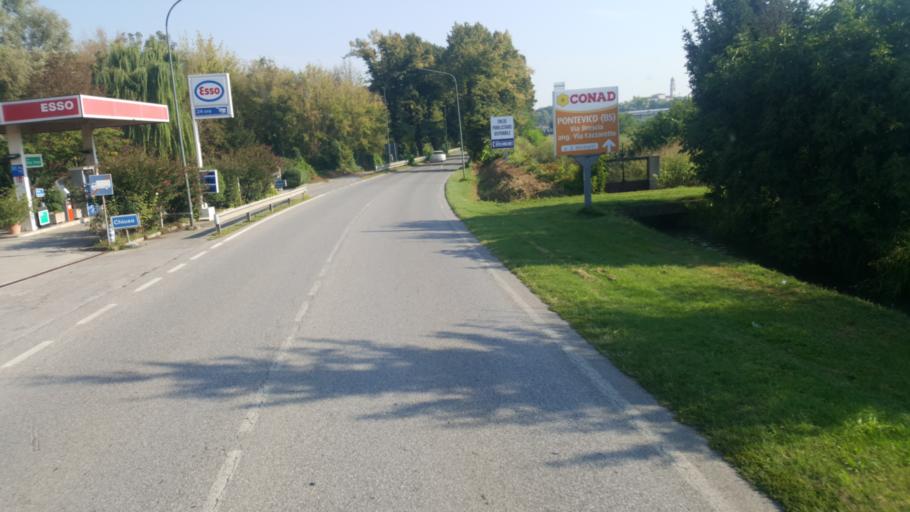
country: IT
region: Lombardy
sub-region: Provincia di Cremona
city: Robecco d'Oglio
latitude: 45.2621
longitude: 10.0779
